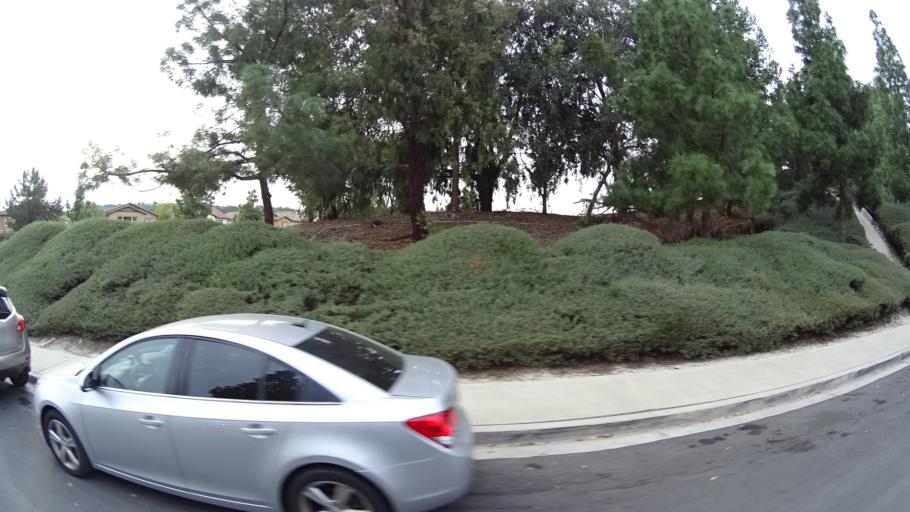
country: US
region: California
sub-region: Orange County
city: Laguna Woods
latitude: 33.5973
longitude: -117.7225
